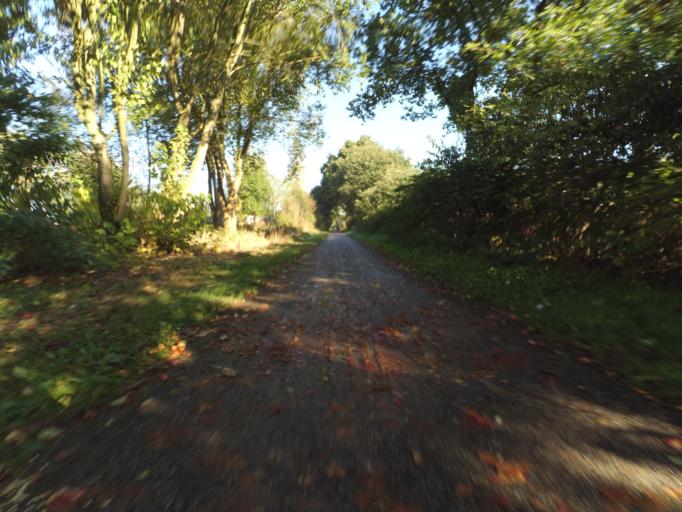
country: NL
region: Gelderland
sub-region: Gemeente Apeldoorn
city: Apeldoorn
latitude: 52.2400
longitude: 5.9624
